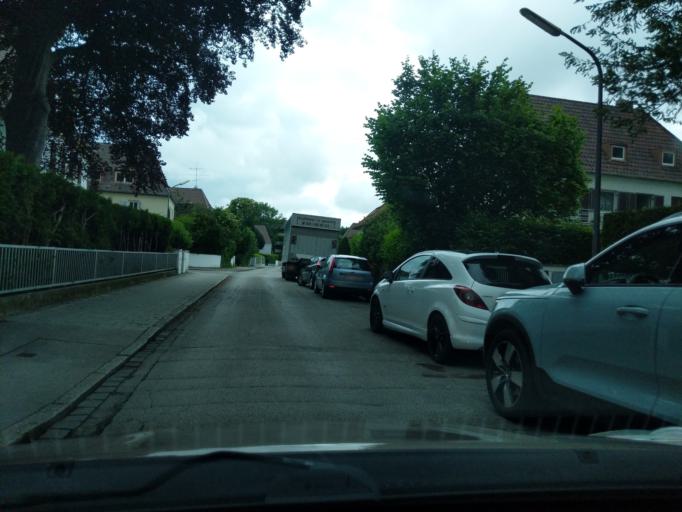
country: DE
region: Bavaria
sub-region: Upper Bavaria
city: Pullach im Isartal
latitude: 48.1112
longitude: 11.5138
